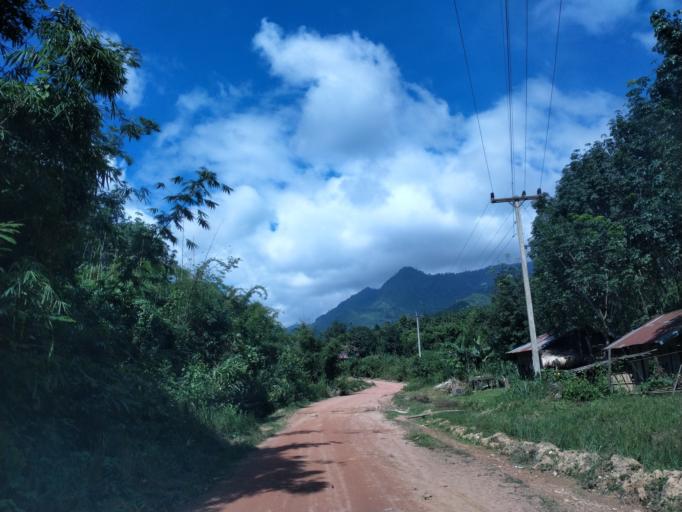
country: TH
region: Nong Khai
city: Rattanawapi
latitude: 18.6367
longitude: 102.9574
